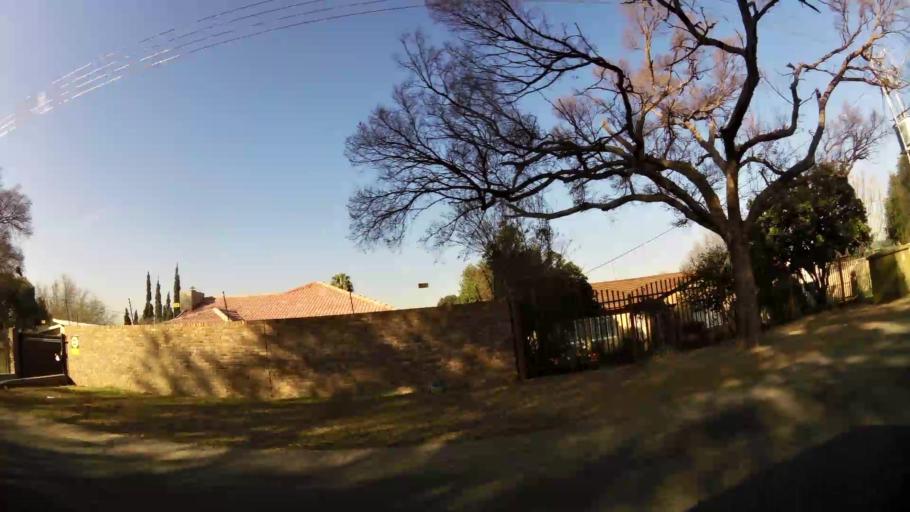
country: ZA
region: Gauteng
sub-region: City of Tshwane Metropolitan Municipality
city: Pretoria
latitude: -25.7027
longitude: 28.1653
